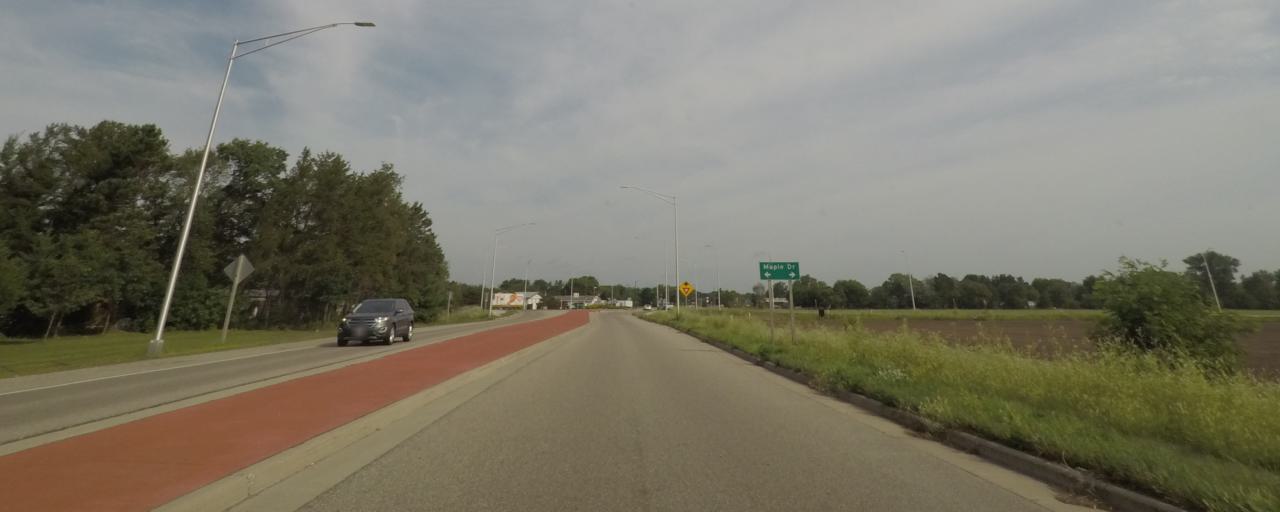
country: US
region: Wisconsin
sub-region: Portage County
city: Plover
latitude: 44.4488
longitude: -89.5432
